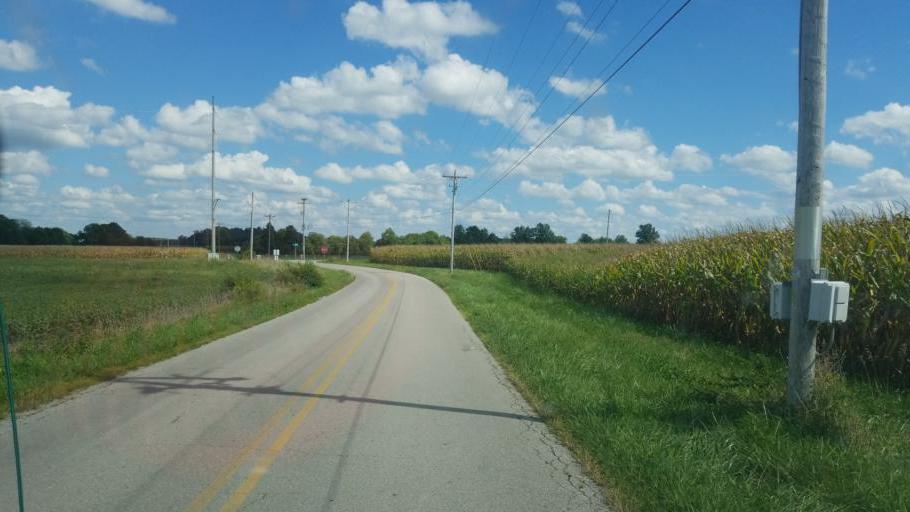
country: US
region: Ohio
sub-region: Delaware County
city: Delaware
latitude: 40.3098
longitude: -83.2006
